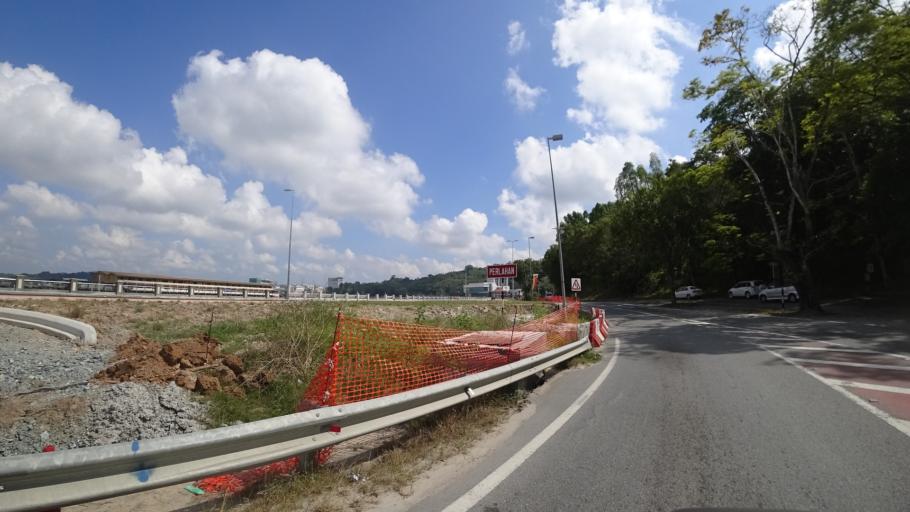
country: BN
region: Brunei and Muara
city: Bandar Seri Begawan
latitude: 4.8800
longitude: 114.9508
